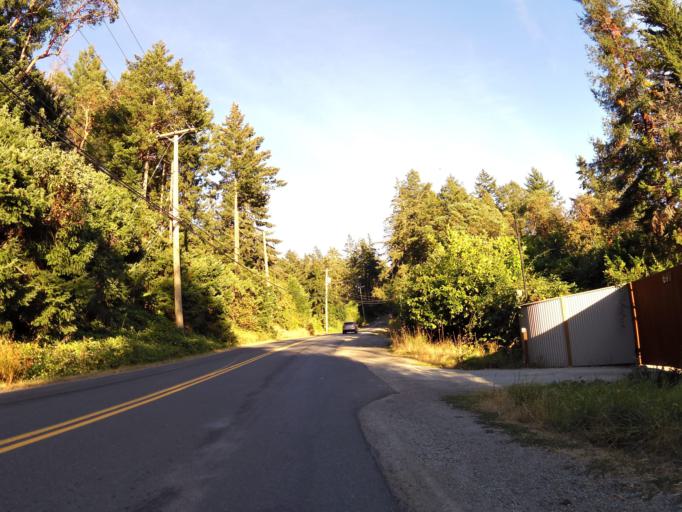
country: CA
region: British Columbia
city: North Cowichan
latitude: 48.8802
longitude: -123.5661
